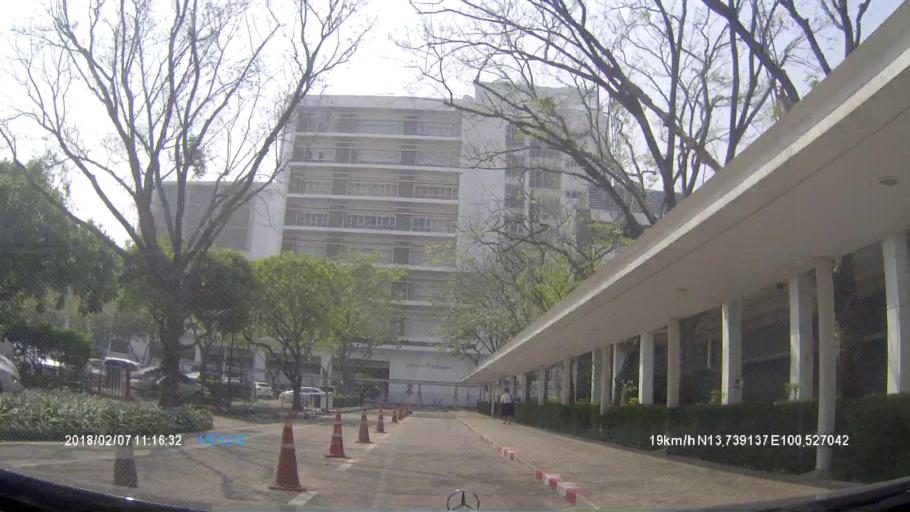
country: TH
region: Bangkok
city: Pathum Wan
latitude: 13.7391
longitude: 100.5270
